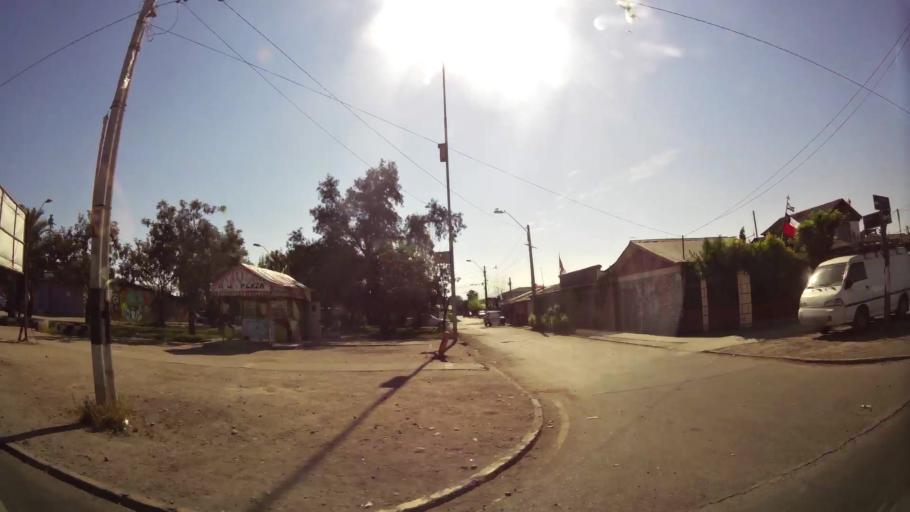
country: CL
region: Santiago Metropolitan
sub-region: Provincia de Maipo
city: San Bernardo
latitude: -33.5170
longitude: -70.6945
